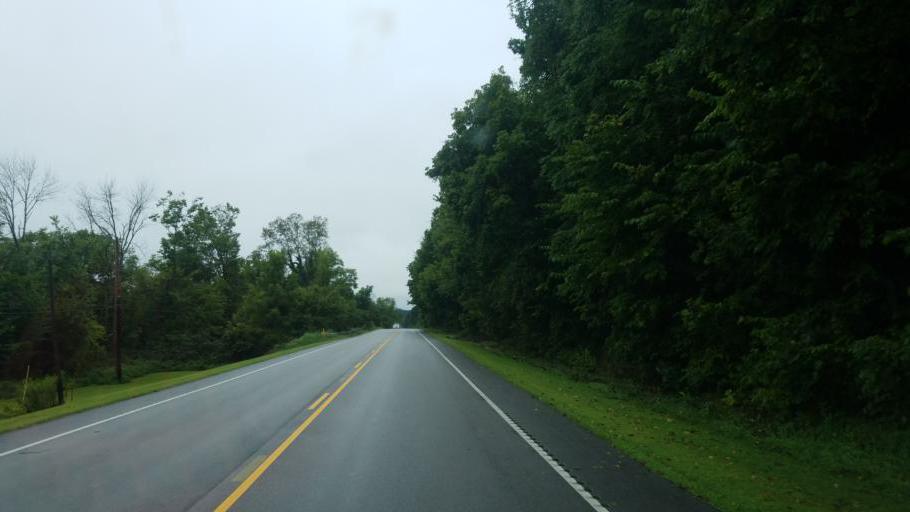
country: US
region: Ohio
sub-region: Adams County
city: Manchester
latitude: 38.6682
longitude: -83.6380
